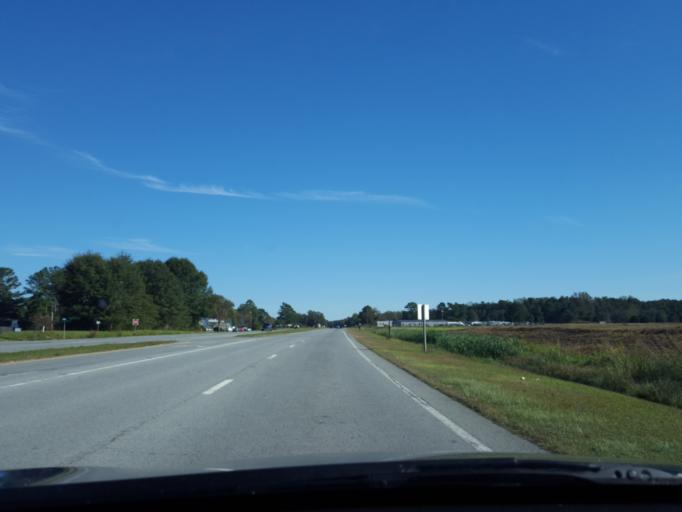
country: US
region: North Carolina
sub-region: Beaufort County
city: Washington
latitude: 35.6177
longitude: -77.1651
